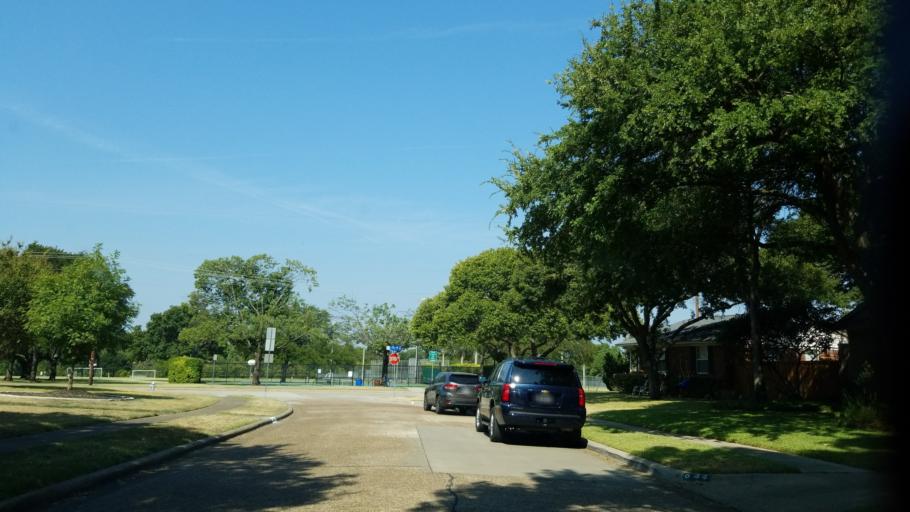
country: US
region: Texas
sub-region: Dallas County
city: Richardson
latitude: 32.9593
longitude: -96.7432
